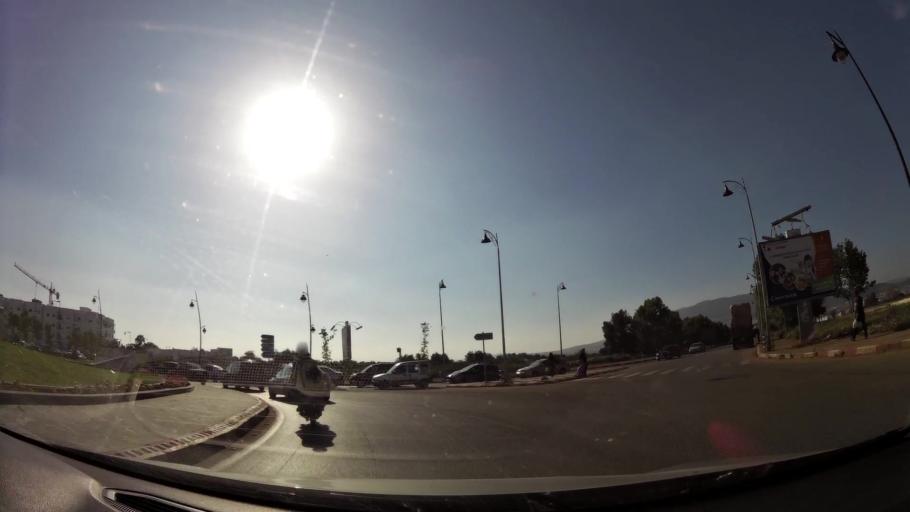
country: MA
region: Fes-Boulemane
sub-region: Fes
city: Fes
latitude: 34.0274
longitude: -5.0276
